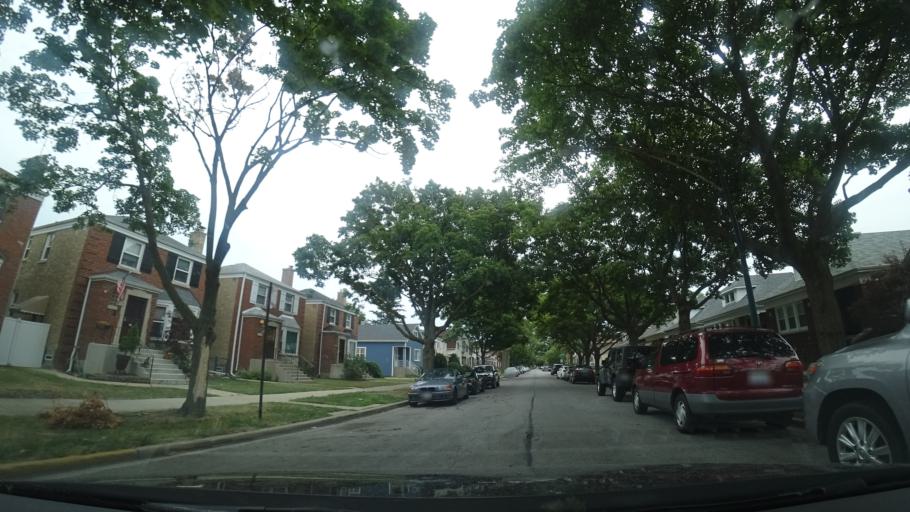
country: US
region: Illinois
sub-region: Cook County
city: Harwood Heights
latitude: 41.9639
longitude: -87.7771
